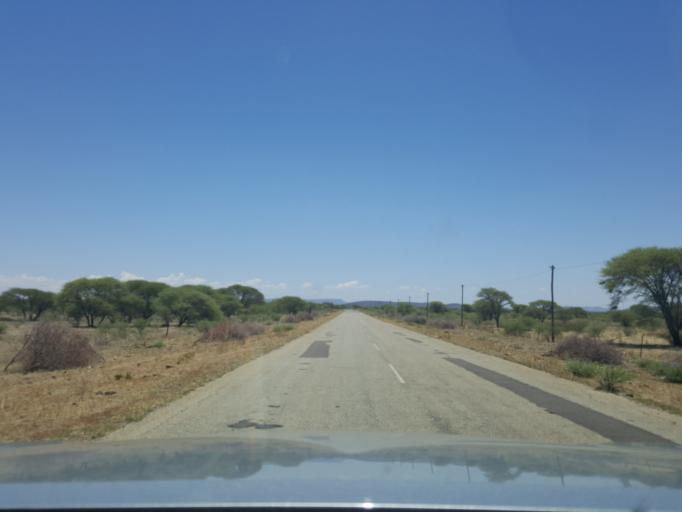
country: BW
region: South East
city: Ramotswa
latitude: -25.0294
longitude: 25.9216
